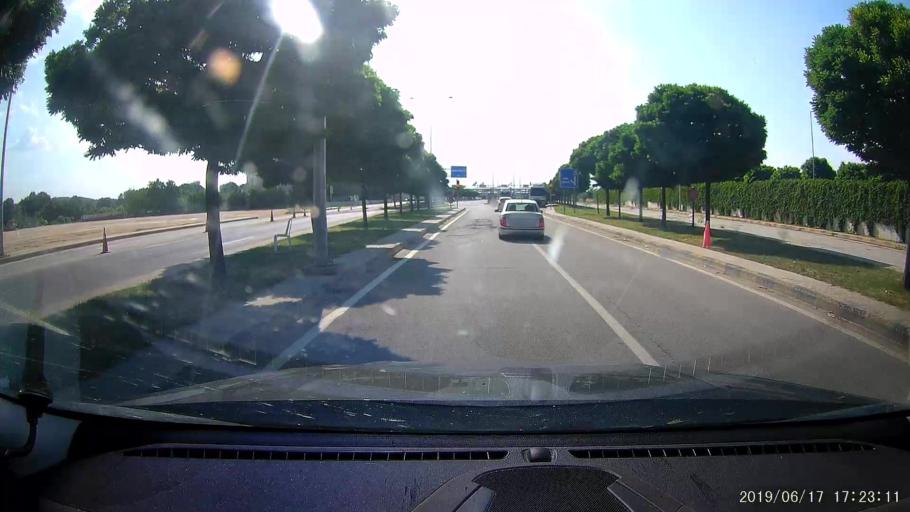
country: GR
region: East Macedonia and Thrace
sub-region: Nomos Evrou
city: Rizia
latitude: 41.7137
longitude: 26.3670
